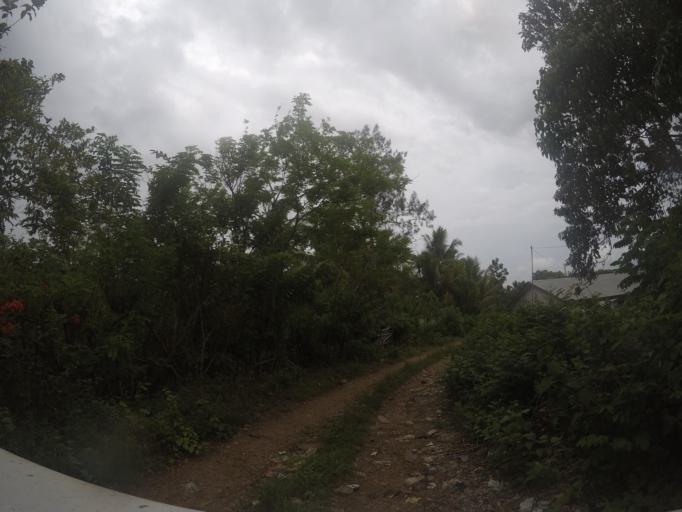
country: TL
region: Lautem
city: Lospalos
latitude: -8.5298
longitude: 126.9930
